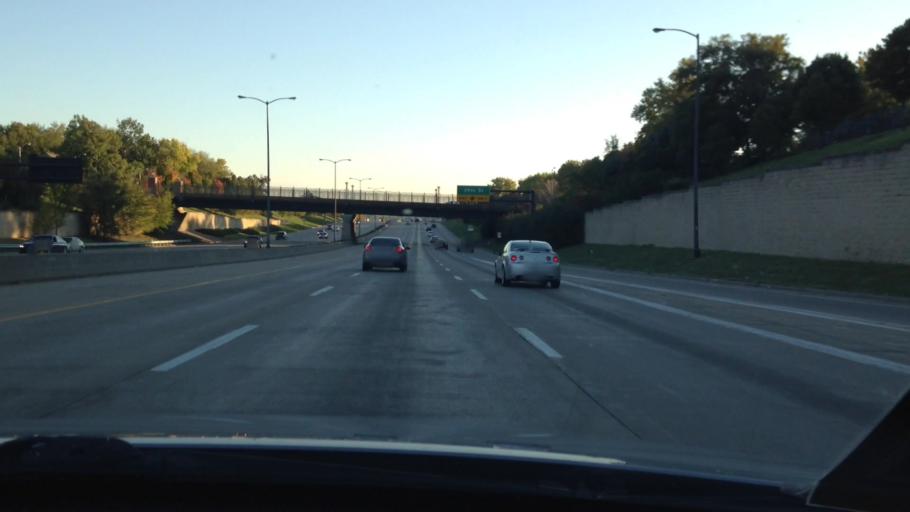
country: US
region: Missouri
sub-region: Jackson County
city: Kansas City
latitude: 39.0645
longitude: -94.5608
